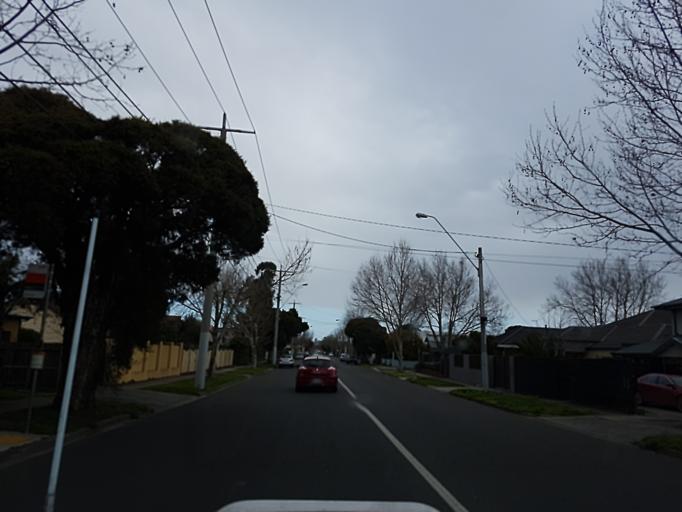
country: AU
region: Victoria
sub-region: Darebin
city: Fairfield
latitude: -37.7734
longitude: 145.0262
